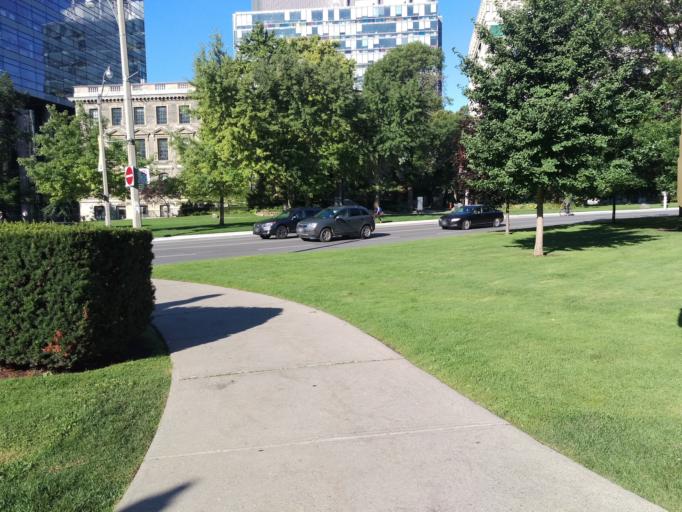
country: CA
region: Ontario
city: Toronto
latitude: 43.6608
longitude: -79.3909
